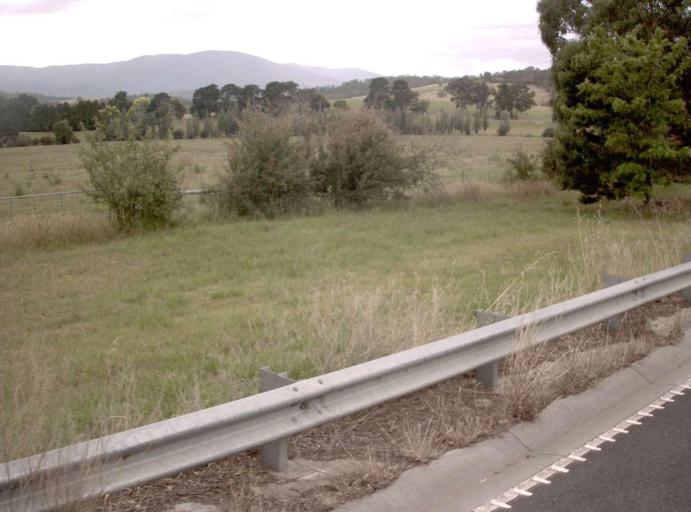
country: AU
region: Victoria
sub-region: Yarra Ranges
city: Badger Creek
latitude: -37.6835
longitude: 145.4633
